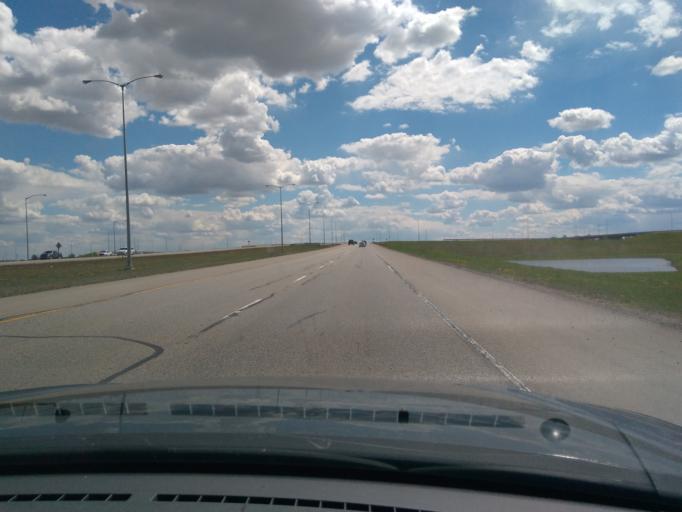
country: CA
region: Alberta
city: Chestermere
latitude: 51.0717
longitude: -113.9207
